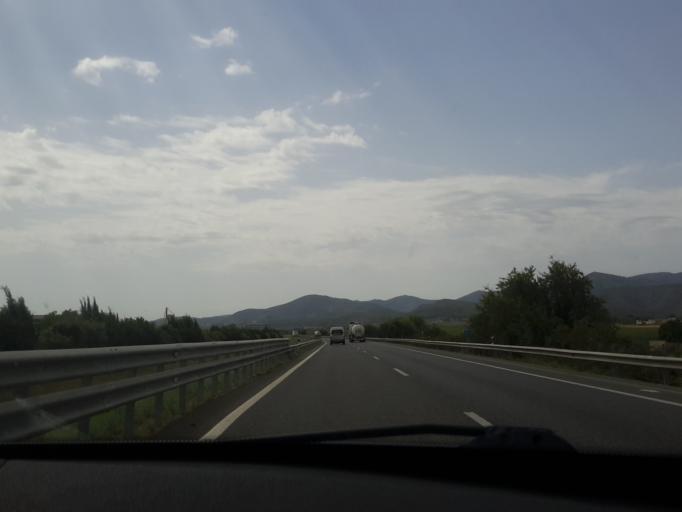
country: ES
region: Catalonia
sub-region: Provincia de Tarragona
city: Santa Oliva
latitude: 41.2721
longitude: 1.5274
